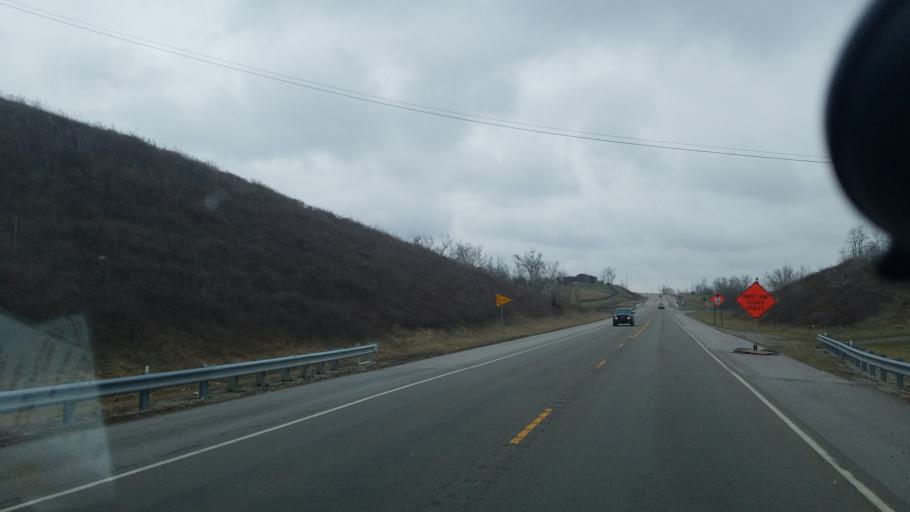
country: US
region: Kentucky
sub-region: Montgomery County
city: Mount Sterling
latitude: 38.1654
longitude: -83.9558
